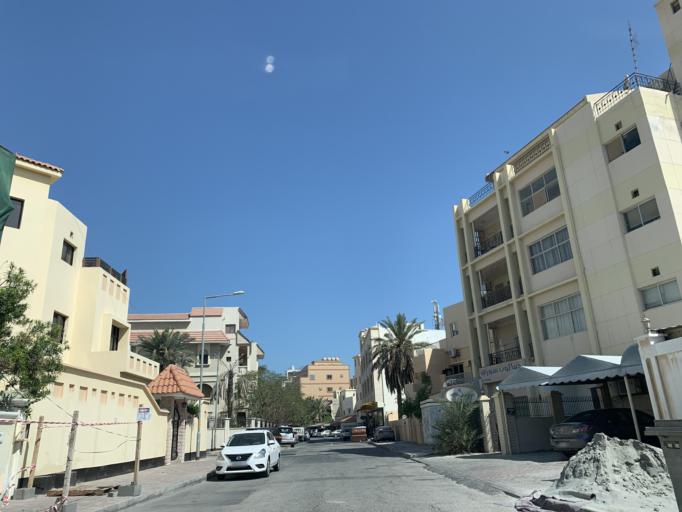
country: BH
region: Manama
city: Manama
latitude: 26.2142
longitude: 50.5802
